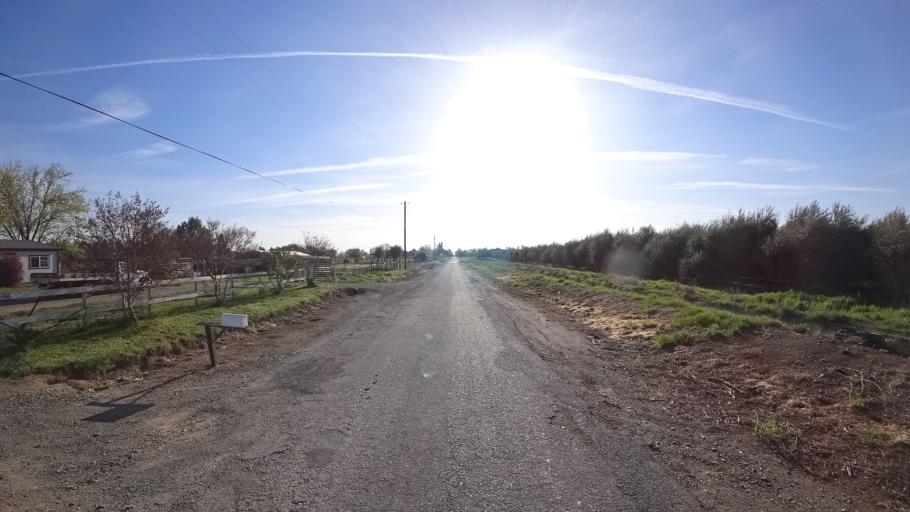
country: US
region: California
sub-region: Glenn County
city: Orland
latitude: 39.7333
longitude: -122.2234
